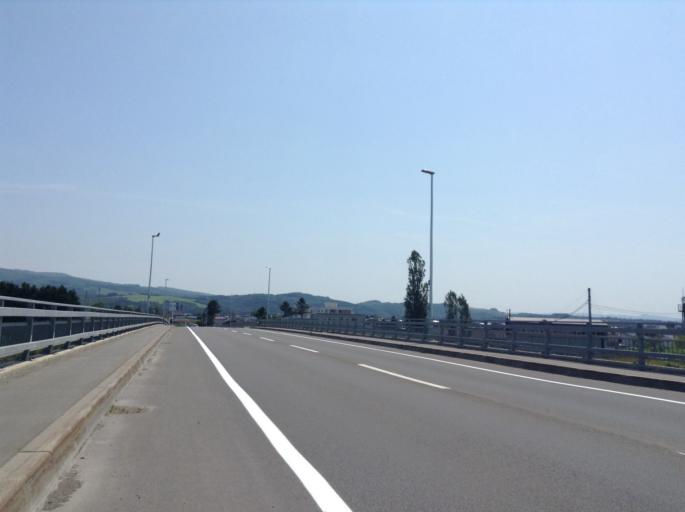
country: JP
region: Hokkaido
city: Nayoro
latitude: 44.3612
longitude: 142.4435
